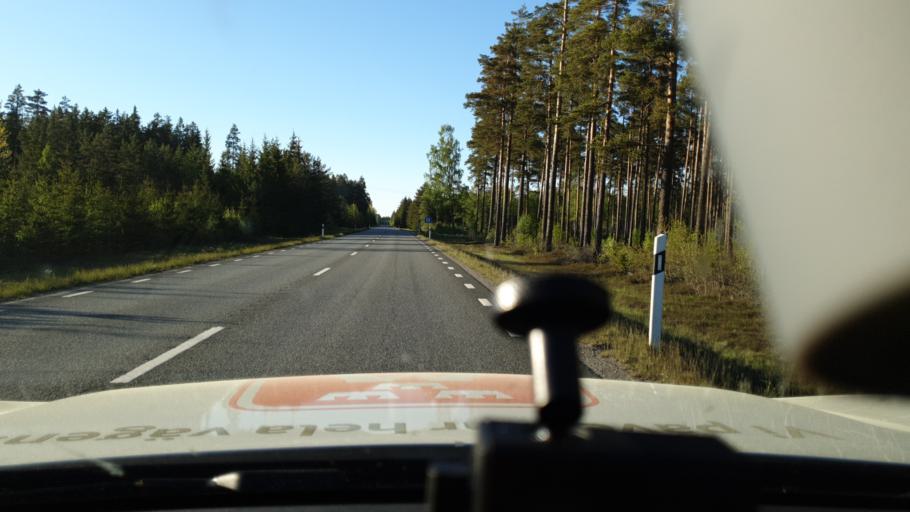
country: SE
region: Joenkoeping
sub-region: Eksjo Kommun
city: Eksjoe
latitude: 57.6174
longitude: 14.9704
